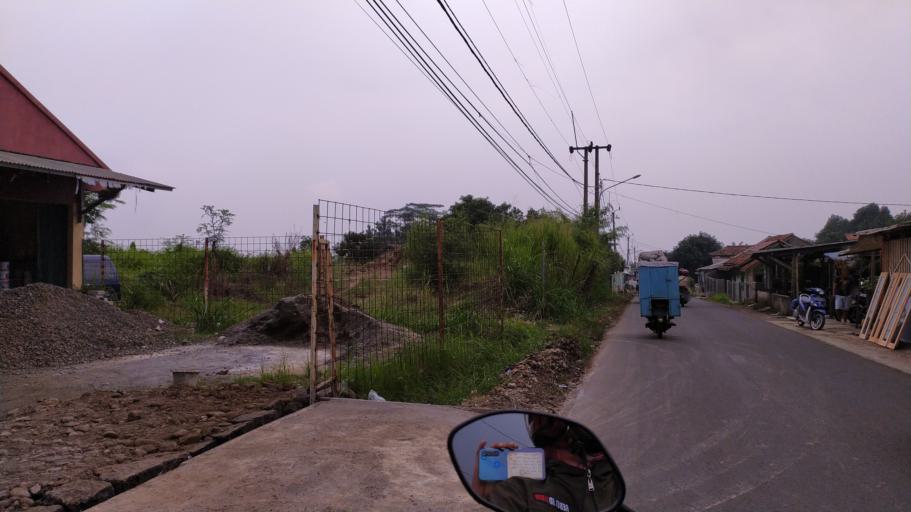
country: ID
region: West Java
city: Ciampea
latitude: -6.5992
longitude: 106.7036
